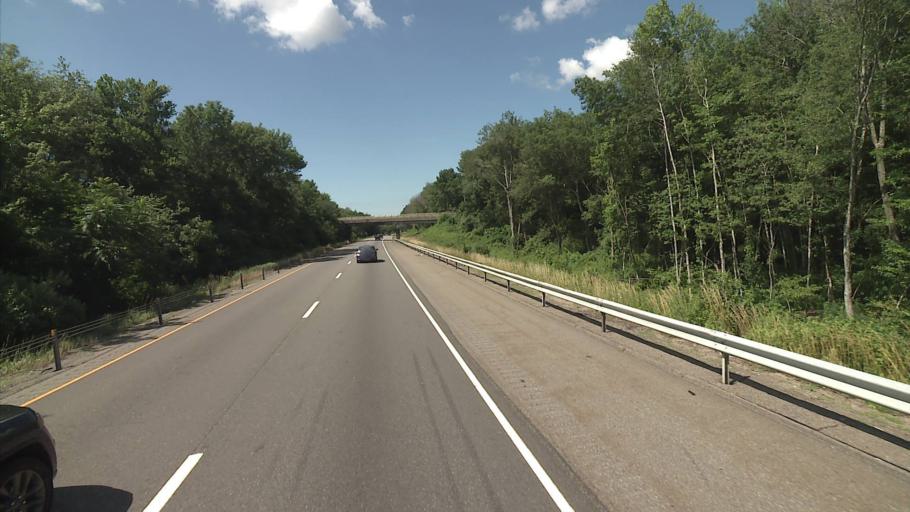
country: US
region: Connecticut
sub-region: New London County
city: Pawcatuck
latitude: 41.3975
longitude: -71.8676
